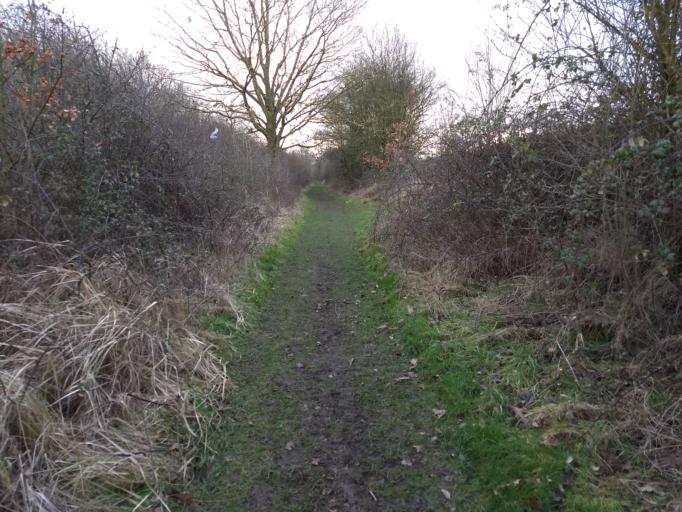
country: GB
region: England
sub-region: Buckinghamshire
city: Bletchley
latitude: 51.9867
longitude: -0.7400
